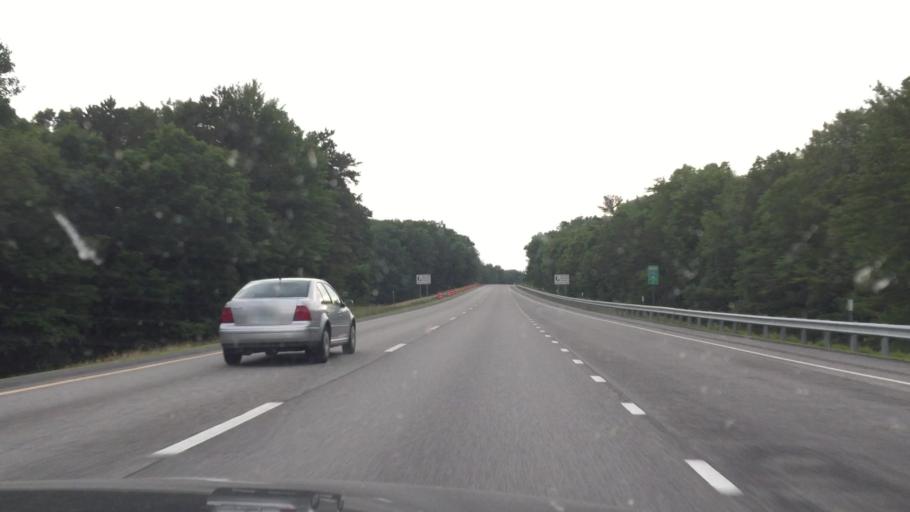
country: US
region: New Hampshire
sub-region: Merrimack County
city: Boscawen
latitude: 43.3350
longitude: -71.6090
